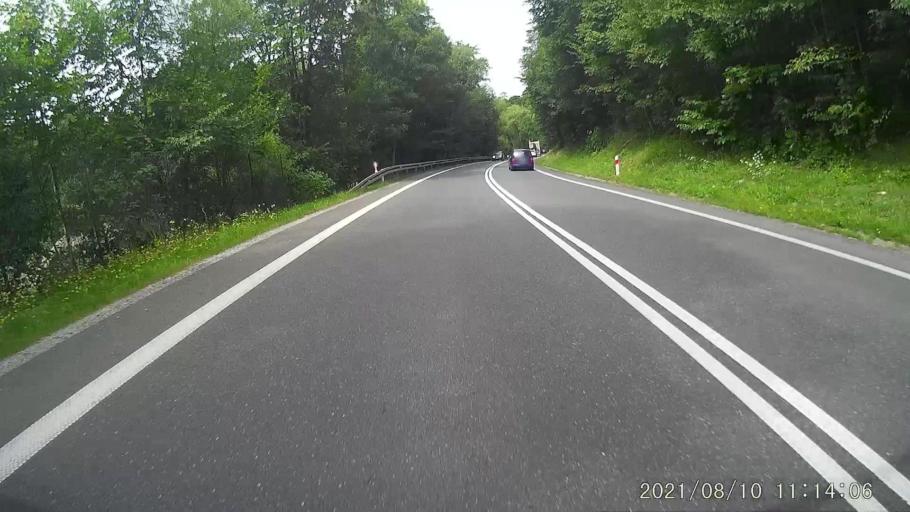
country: PL
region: Lower Silesian Voivodeship
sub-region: Powiat klodzki
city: Szczytna
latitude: 50.4109
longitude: 16.4253
